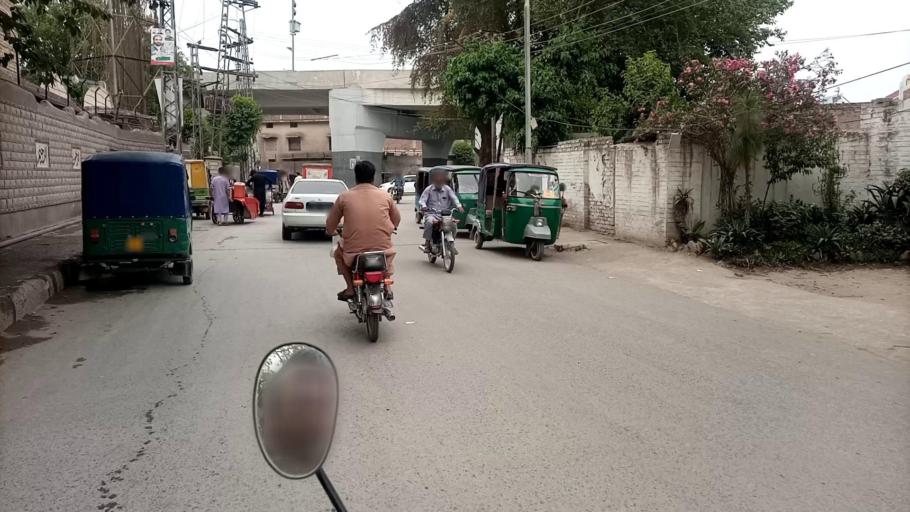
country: PK
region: Khyber Pakhtunkhwa
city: Peshawar
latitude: 33.9939
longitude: 71.5370
